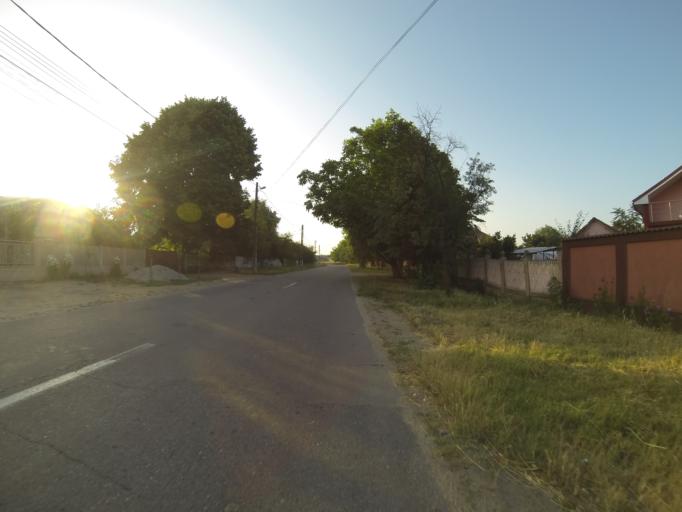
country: RO
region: Dolj
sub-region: Comuna Dobrotesti
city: Dobrotesti
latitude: 43.9630
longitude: 24.1067
